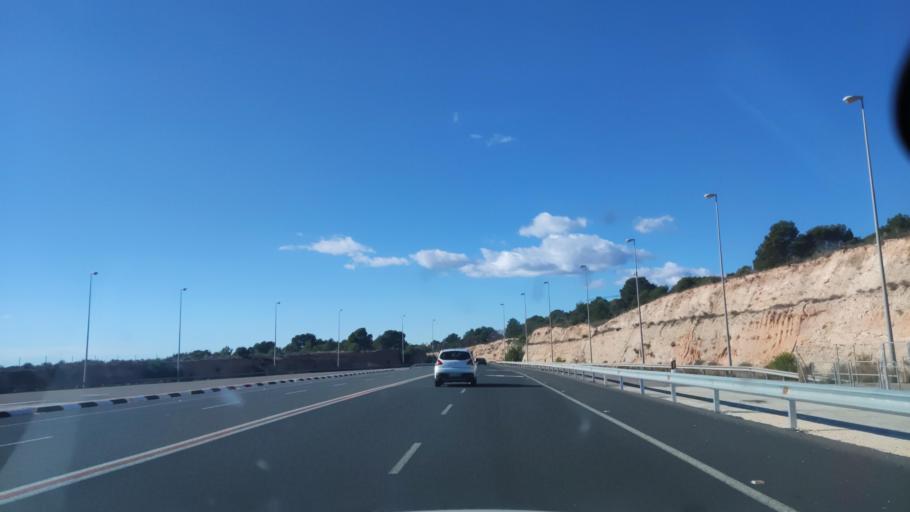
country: ES
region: Valencia
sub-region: Provincia de Alicante
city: Benidorm
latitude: 38.5484
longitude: -0.1682
